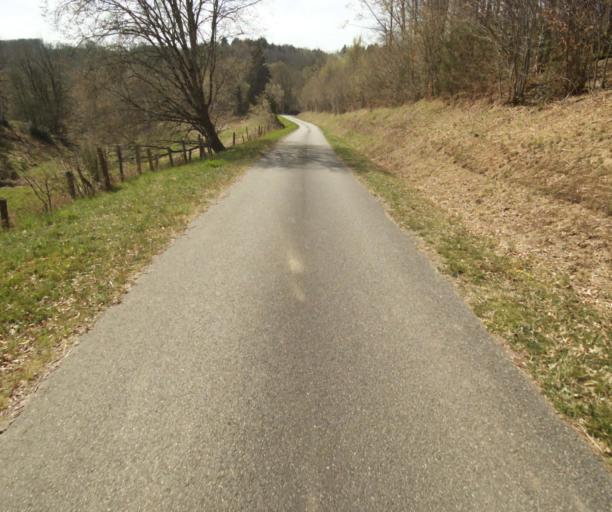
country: FR
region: Limousin
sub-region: Departement de la Correze
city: Seilhac
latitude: 45.4019
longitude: 1.7827
